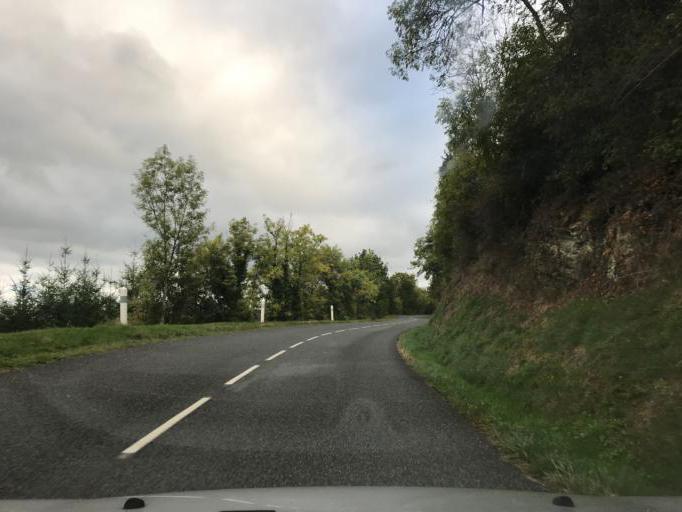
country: FR
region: Rhone-Alpes
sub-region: Departement du Rhone
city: Cogny
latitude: 46.0155
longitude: 4.5826
